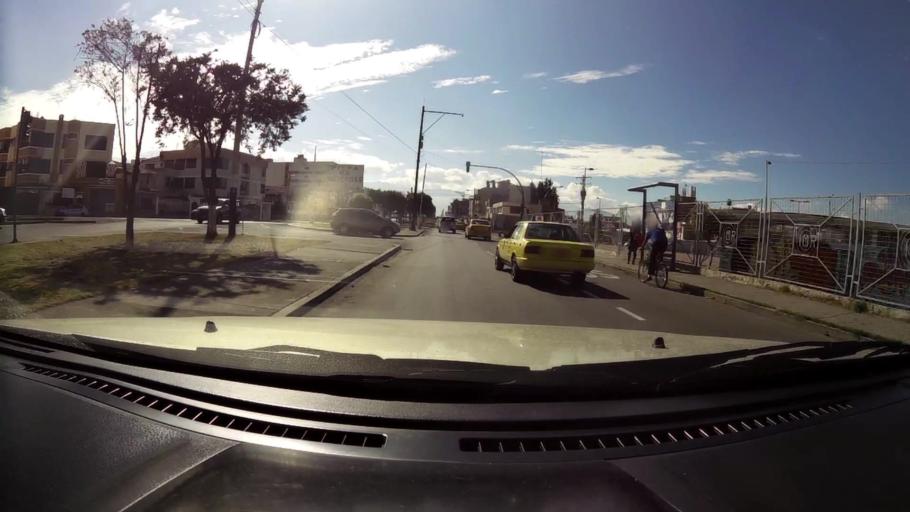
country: EC
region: Chimborazo
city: Riobamba
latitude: -1.6572
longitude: -78.6692
